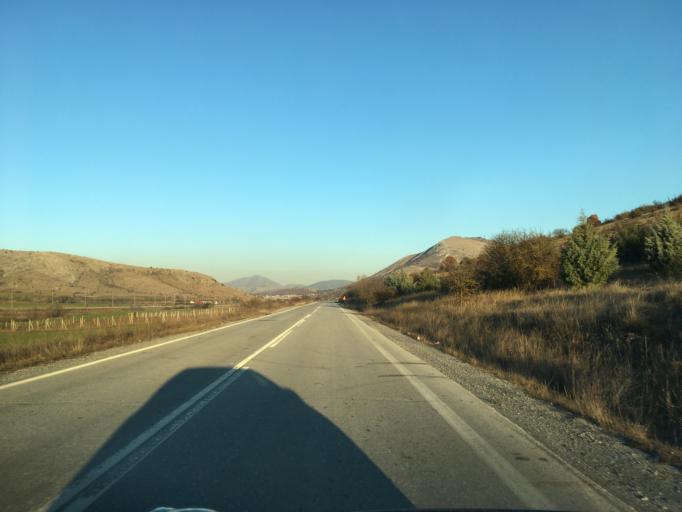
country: GR
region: West Macedonia
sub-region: Nomos Kozanis
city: Kozani
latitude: 40.3170
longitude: 21.7425
